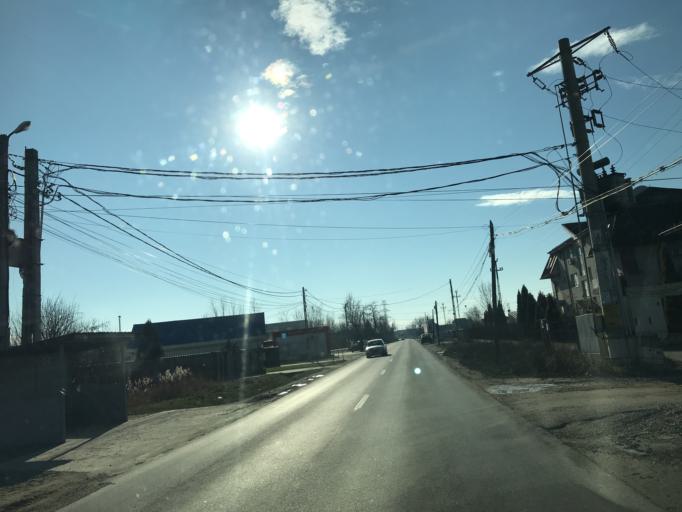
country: RO
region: Olt
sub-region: Comuna Slatioara
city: Slatioara
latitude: 44.4165
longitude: 24.3269
